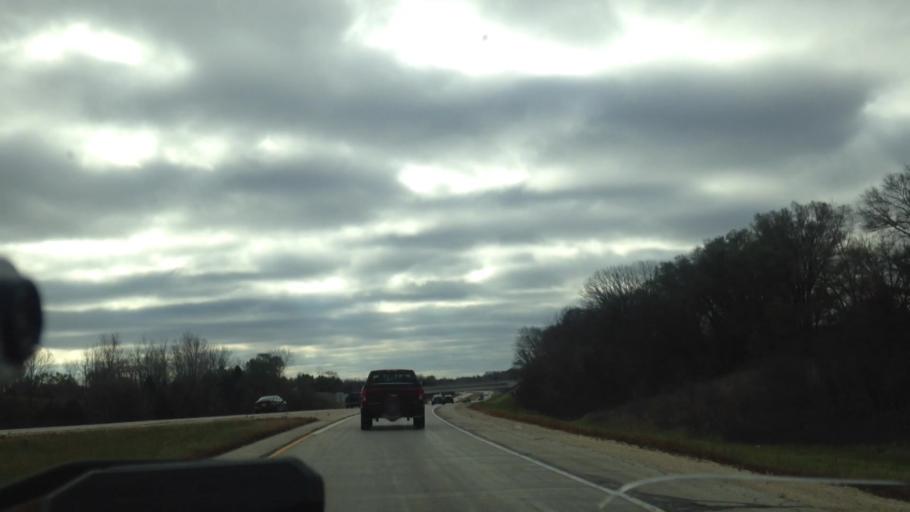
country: US
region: Wisconsin
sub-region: Washington County
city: West Bend
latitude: 43.4251
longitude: -88.2087
